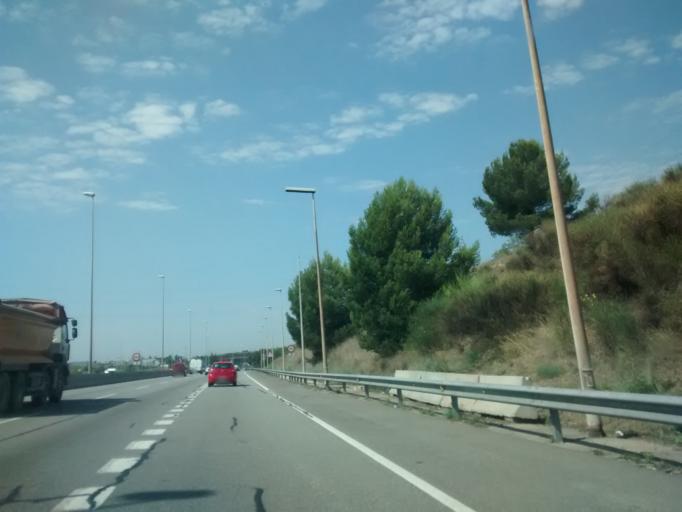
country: ES
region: Catalonia
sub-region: Provincia de Barcelona
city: Barbera del Valles
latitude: 41.4987
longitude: 2.1153
